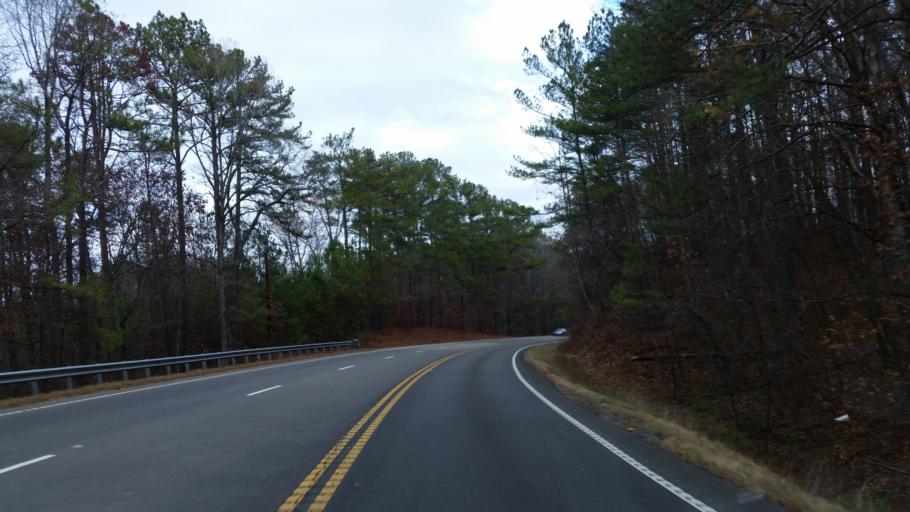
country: US
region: Georgia
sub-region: Cherokee County
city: Holly Springs
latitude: 34.2165
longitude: -84.5822
